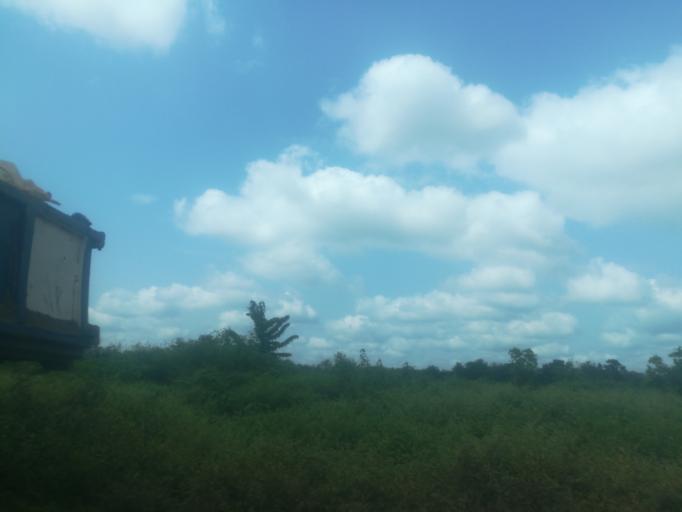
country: NG
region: Oyo
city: Moniya
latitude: 7.5503
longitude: 3.9103
